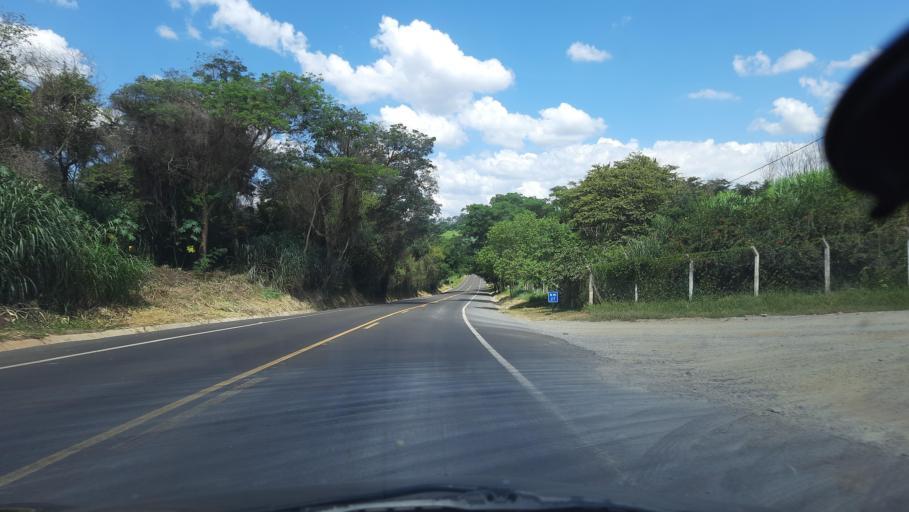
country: BR
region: Sao Paulo
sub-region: Sao Jose Do Rio Pardo
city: Sao Jose do Rio Pardo
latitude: -21.5944
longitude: -46.9879
